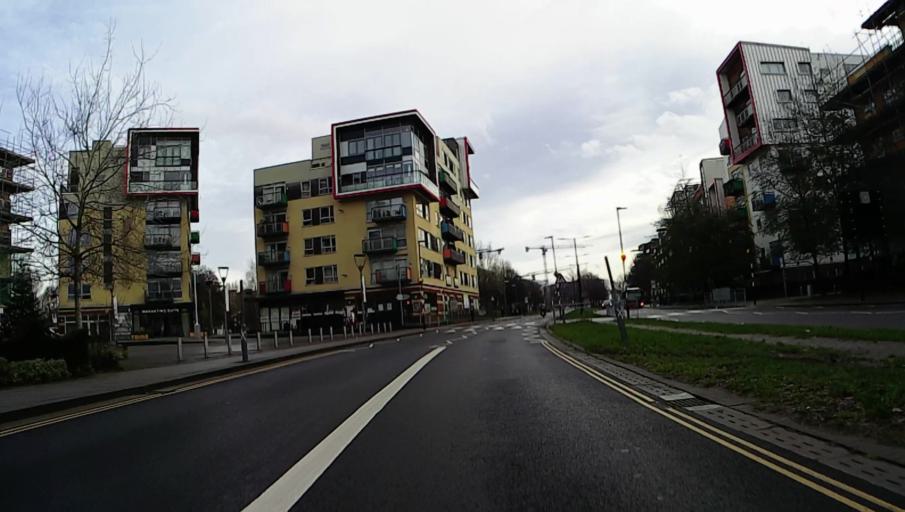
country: GB
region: England
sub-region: Greater London
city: Blackheath
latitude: 51.4947
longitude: 0.0128
